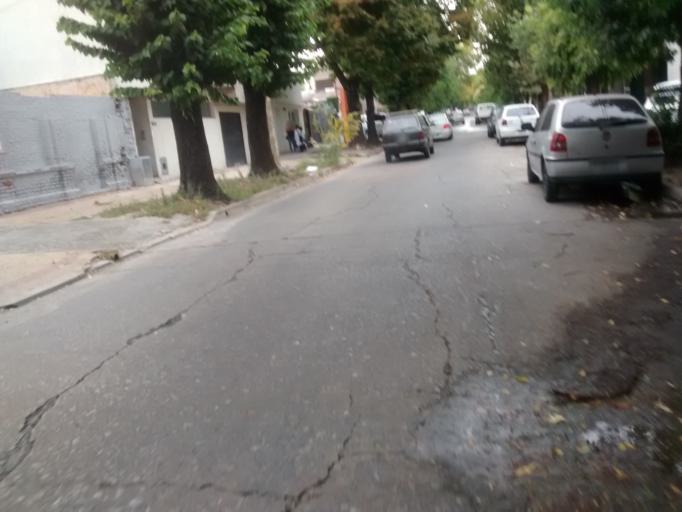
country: AR
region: Buenos Aires
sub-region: Partido de La Plata
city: La Plata
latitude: -34.9392
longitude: -57.9513
